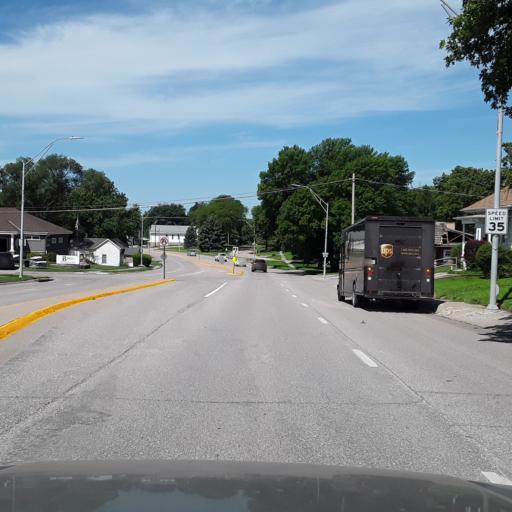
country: US
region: Nebraska
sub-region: Seward County
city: Seward
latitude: 40.9070
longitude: -97.1017
